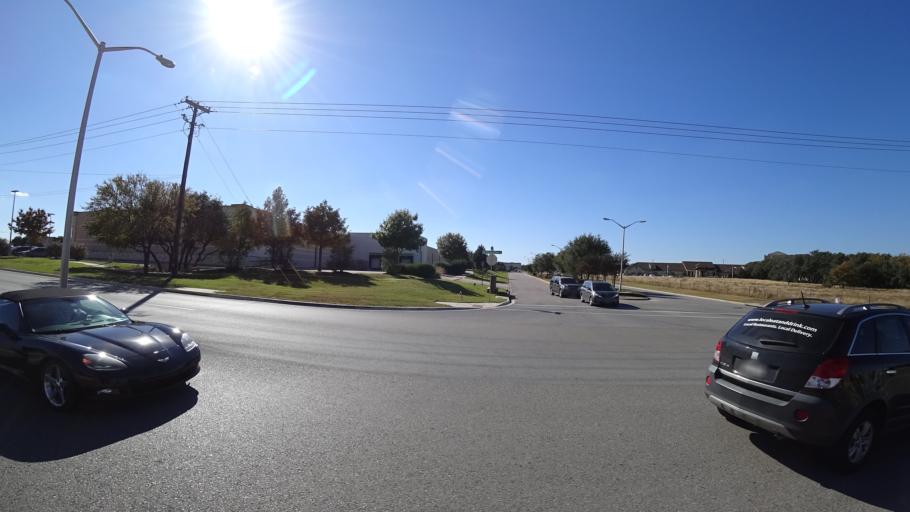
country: US
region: Texas
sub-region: Williamson County
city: Cedar Park
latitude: 30.5301
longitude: -97.8065
